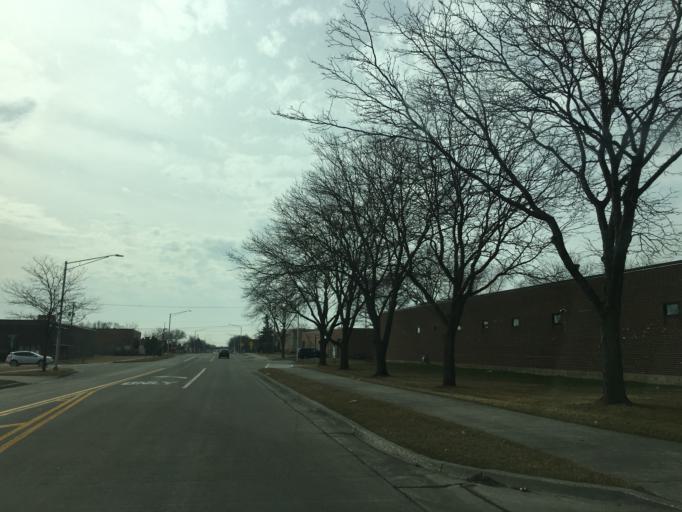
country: US
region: Illinois
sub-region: DuPage County
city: Roselle
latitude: 42.0035
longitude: -88.1016
